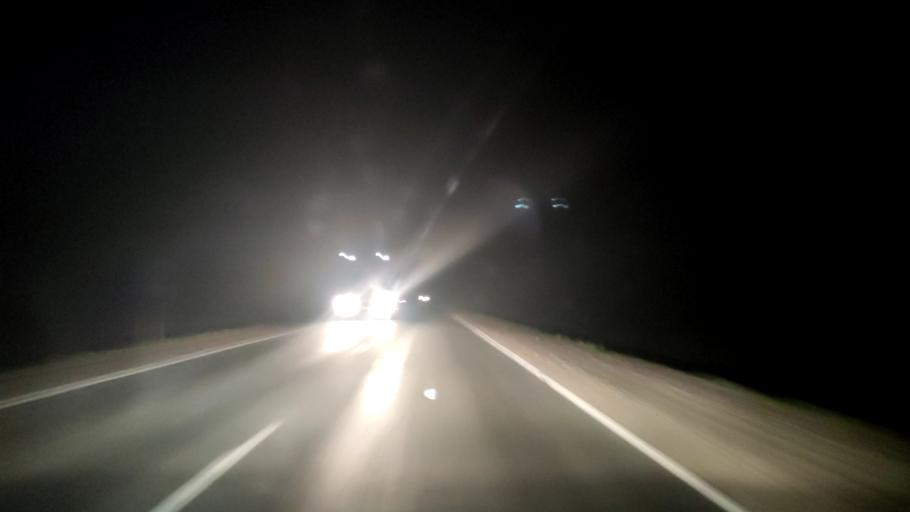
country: RU
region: Voronezj
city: Nizhnedevitsk
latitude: 51.5680
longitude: 38.2767
